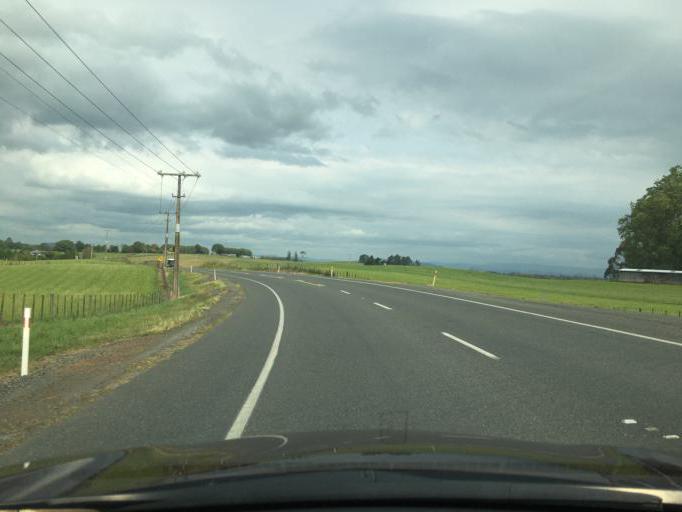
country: NZ
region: Waikato
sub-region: Waipa District
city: Cambridge
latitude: -38.0135
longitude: 175.3556
